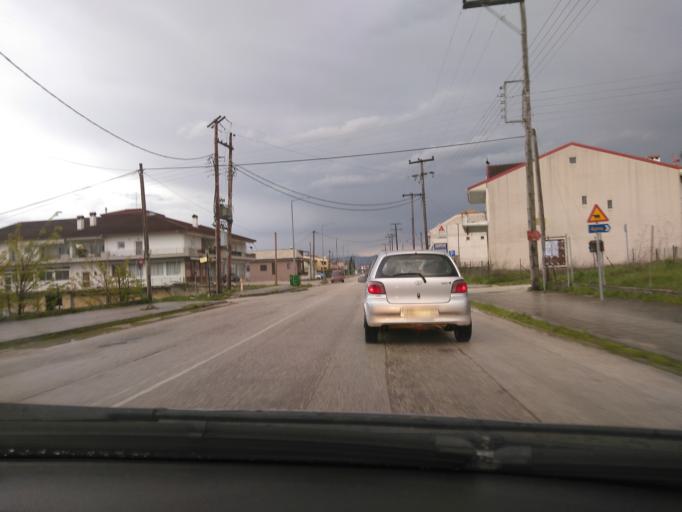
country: GR
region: Epirus
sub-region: Nomos Ioanninon
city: Anatoli
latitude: 39.6357
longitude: 20.8720
